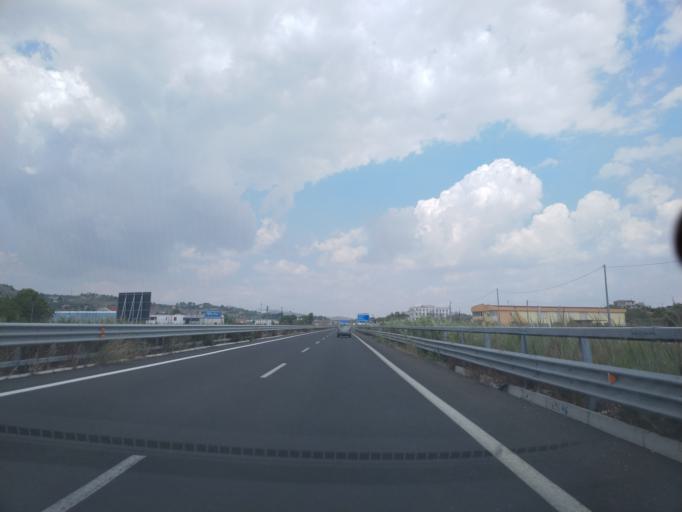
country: IT
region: Sicily
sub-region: Agrigento
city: Racalmuto
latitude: 37.3802
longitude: 13.7288
